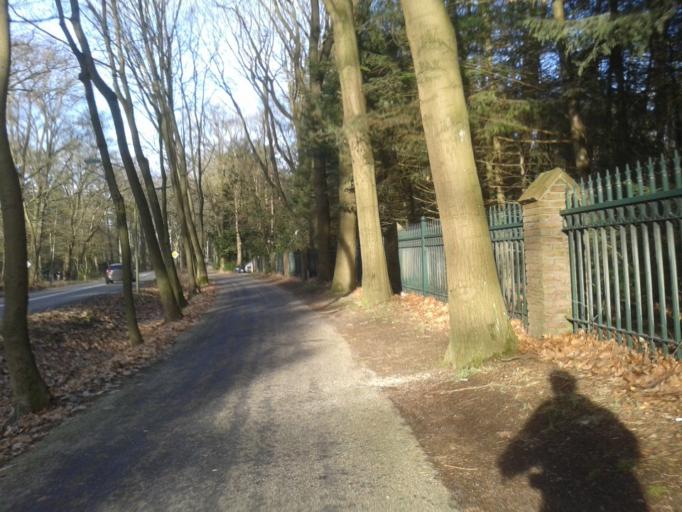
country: NL
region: North Brabant
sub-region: Gemeente Oisterwijk
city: Oisterwijk
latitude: 51.5577
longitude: 5.1748
